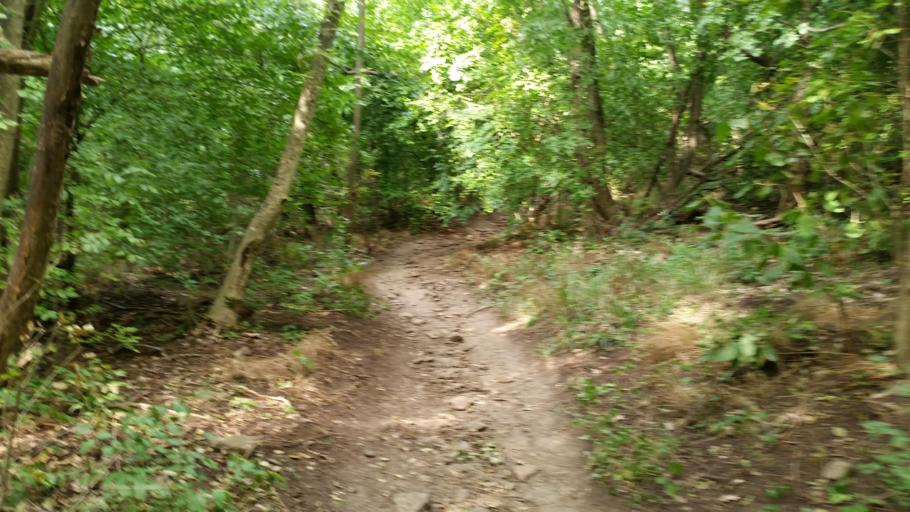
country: HU
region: Veszprem
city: Tihany
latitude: 46.9128
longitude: 17.8538
